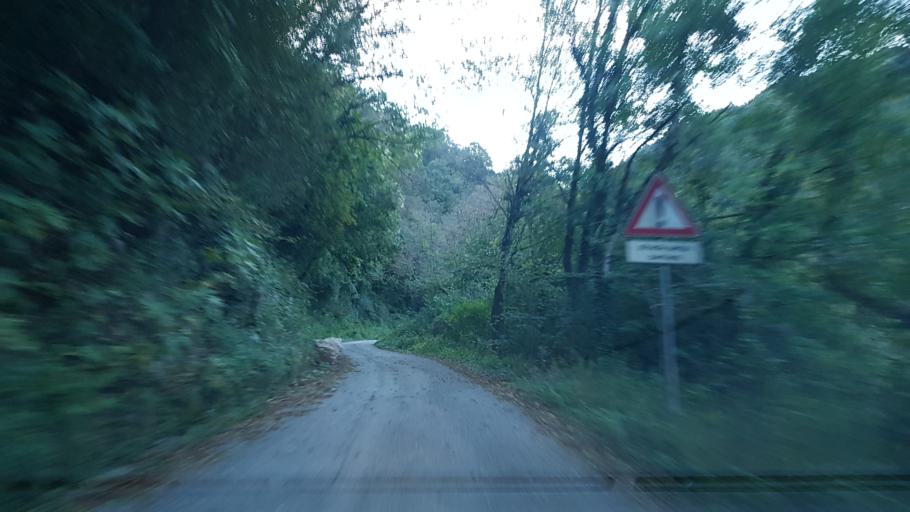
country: IT
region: Friuli Venezia Giulia
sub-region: Provincia di Udine
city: Venzone
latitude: 46.3343
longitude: 13.1500
